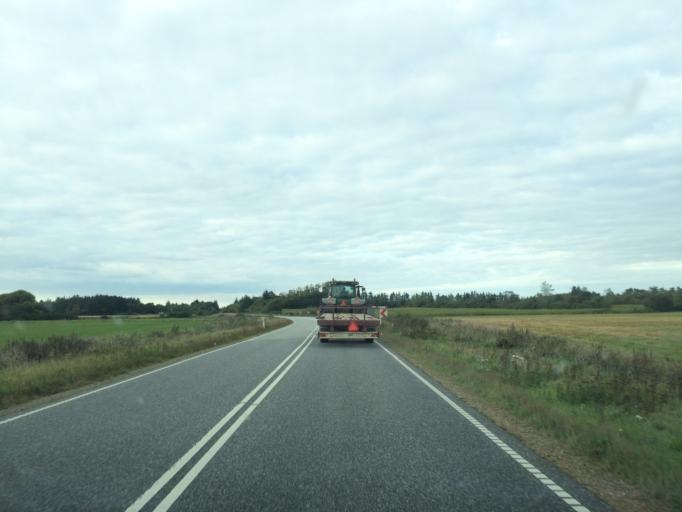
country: DK
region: Central Jutland
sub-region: Holstebro Kommune
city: Ulfborg
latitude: 56.2112
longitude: 8.3065
